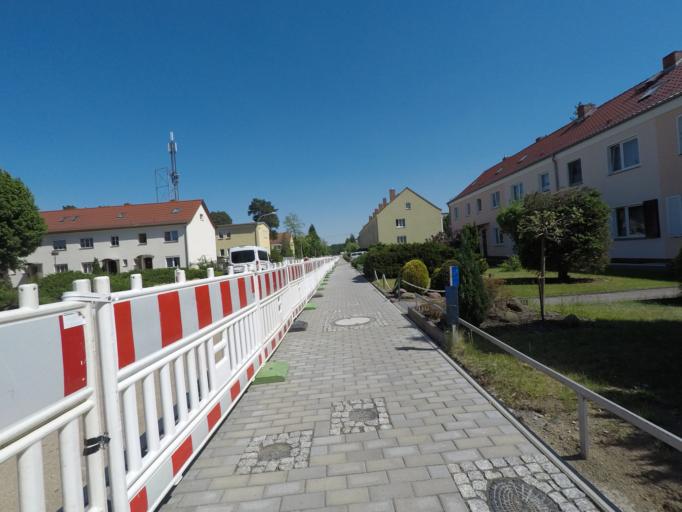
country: DE
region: Brandenburg
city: Melchow
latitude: 52.8368
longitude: 13.7437
